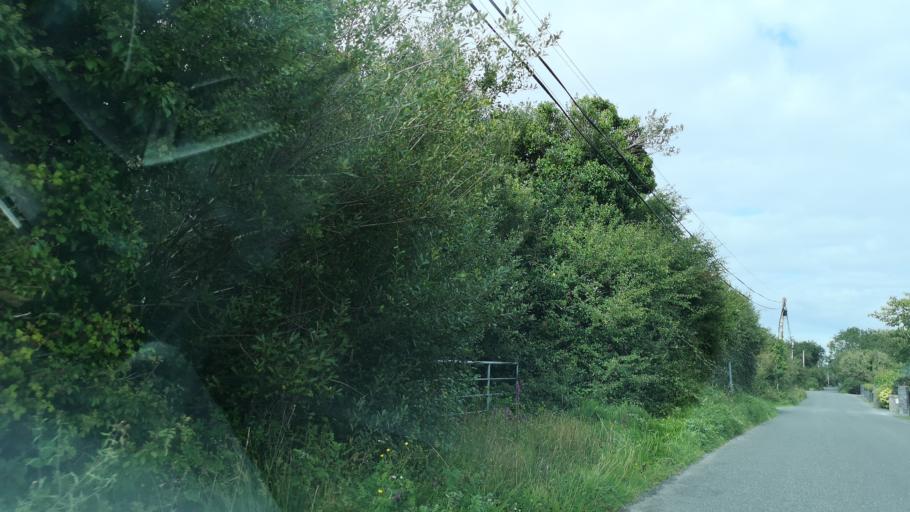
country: IE
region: Connaught
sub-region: County Galway
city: Moycullen
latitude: 53.3172
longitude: -9.1505
